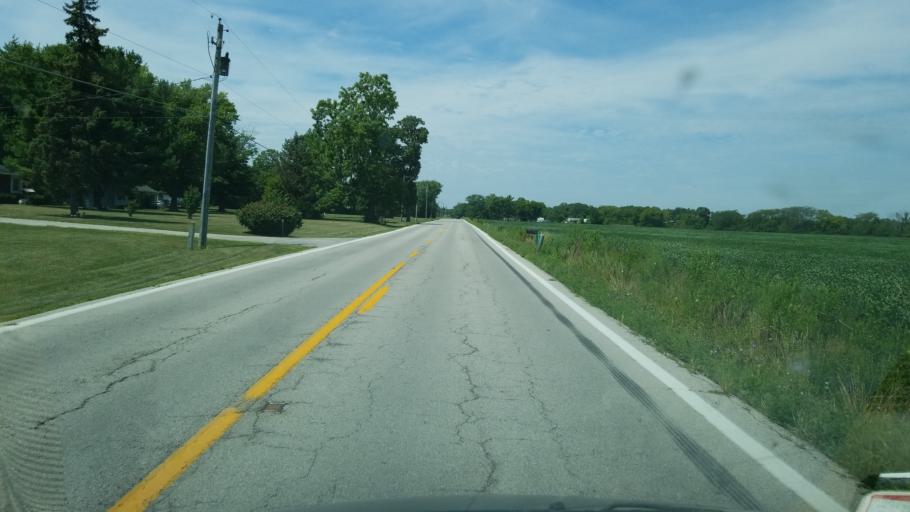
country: US
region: Ohio
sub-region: Madison County
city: West Jefferson
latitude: 39.8567
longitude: -83.2353
